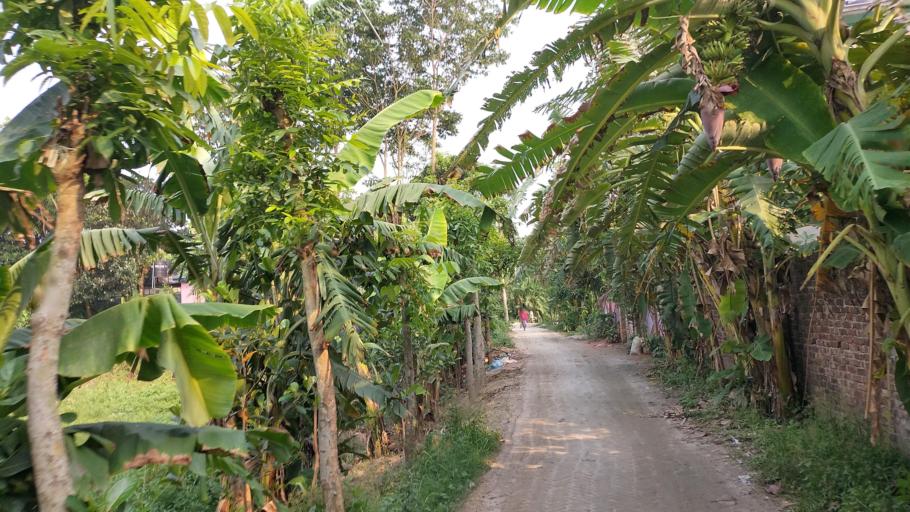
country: BD
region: Dhaka
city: Azimpur
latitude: 23.6696
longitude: 90.3145
